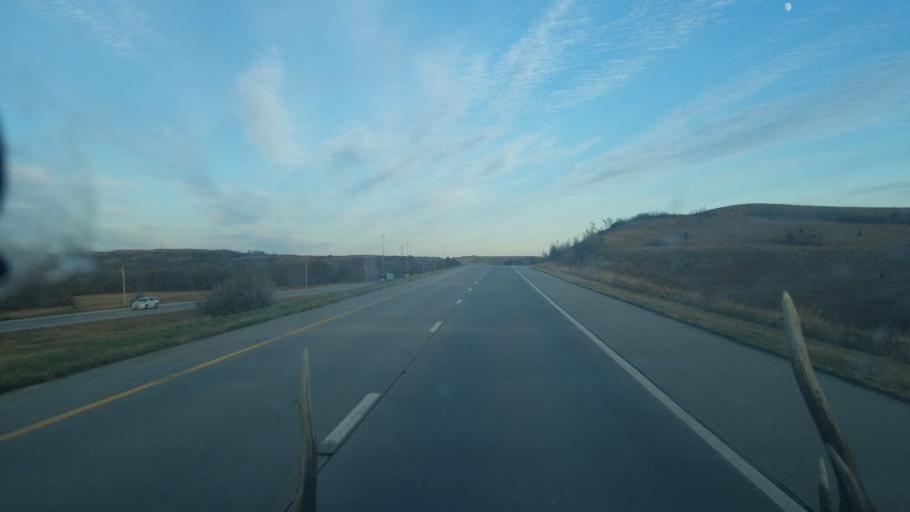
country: US
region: Kansas
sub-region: Riley County
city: Ogden
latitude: 39.0668
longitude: -96.6293
